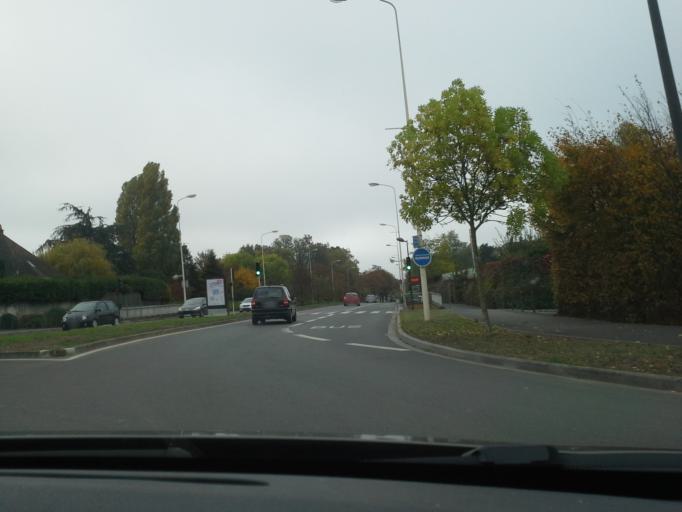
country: FR
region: Centre
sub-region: Departement d'Indre-et-Loire
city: Tours
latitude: 47.4189
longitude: 0.7044
